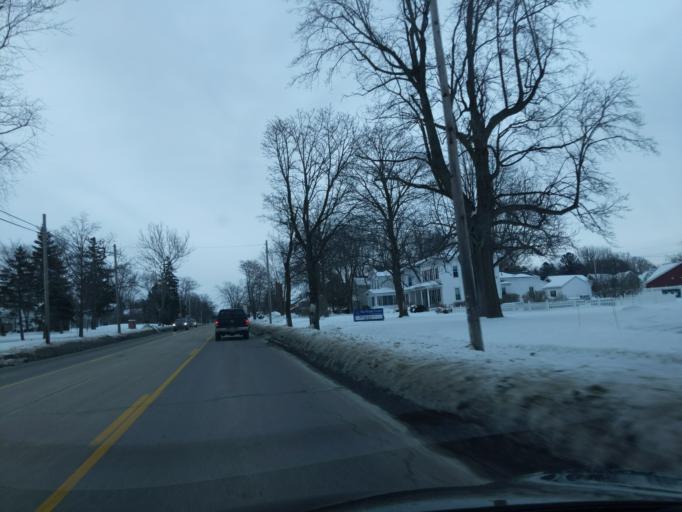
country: US
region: Michigan
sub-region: Ottawa County
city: Spring Lake
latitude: 43.0767
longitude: -86.1933
